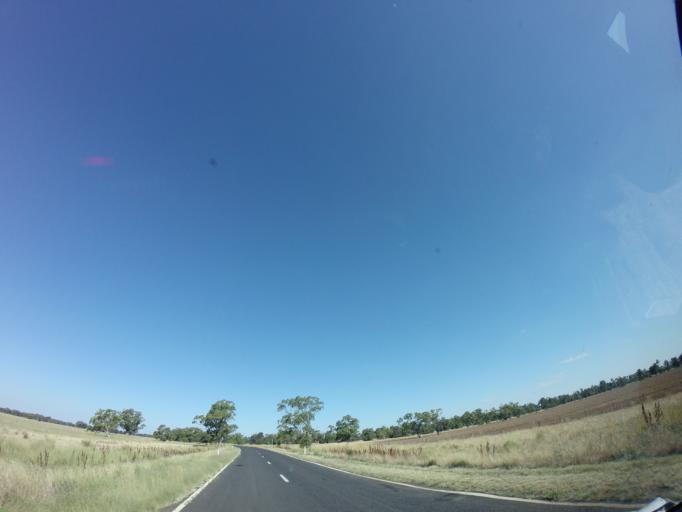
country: AU
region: New South Wales
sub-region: Gilgandra
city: Gilgandra
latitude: -31.6723
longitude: 148.2346
